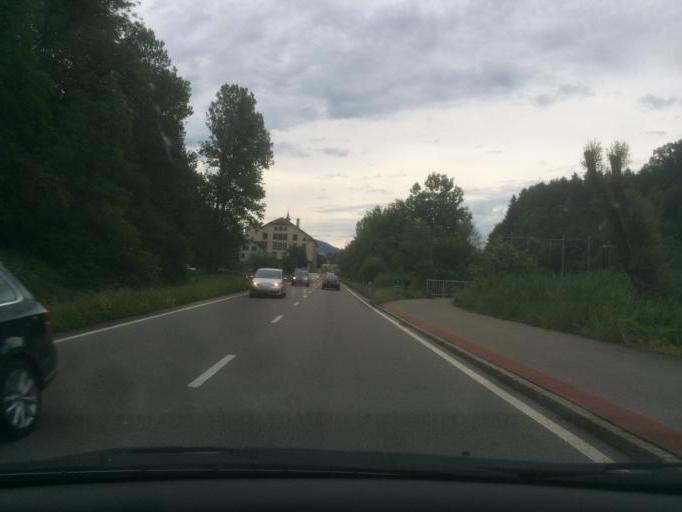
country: CH
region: Zurich
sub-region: Bezirk Hinwil
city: Wetzikon / Robenhausen
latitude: 47.3315
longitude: 8.7745
